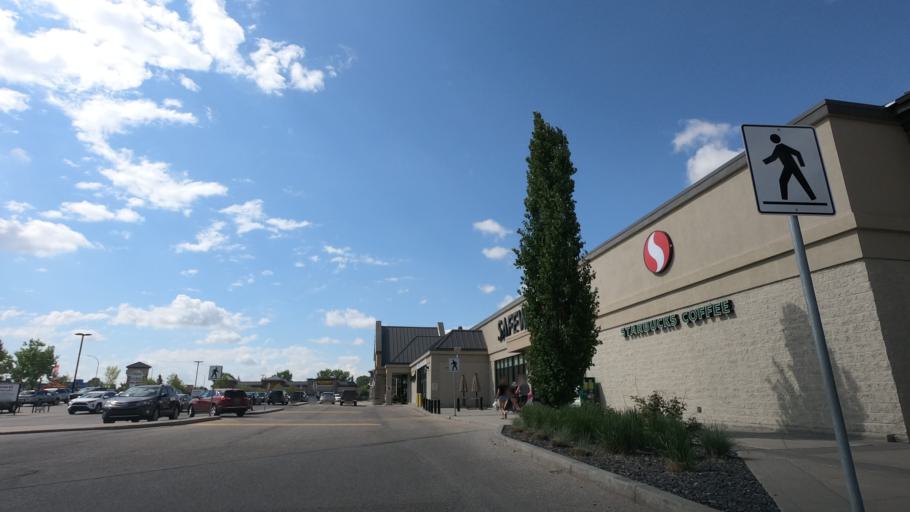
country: CA
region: Alberta
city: Airdrie
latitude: 51.2882
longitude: -114.0147
